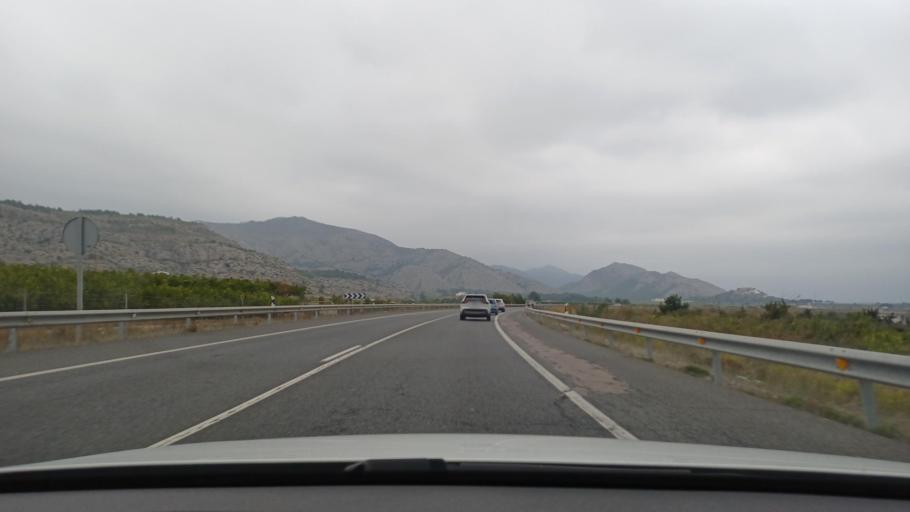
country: ES
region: Valencia
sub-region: Provincia de Castello
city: Borriol
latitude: 40.0266
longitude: -0.0339
